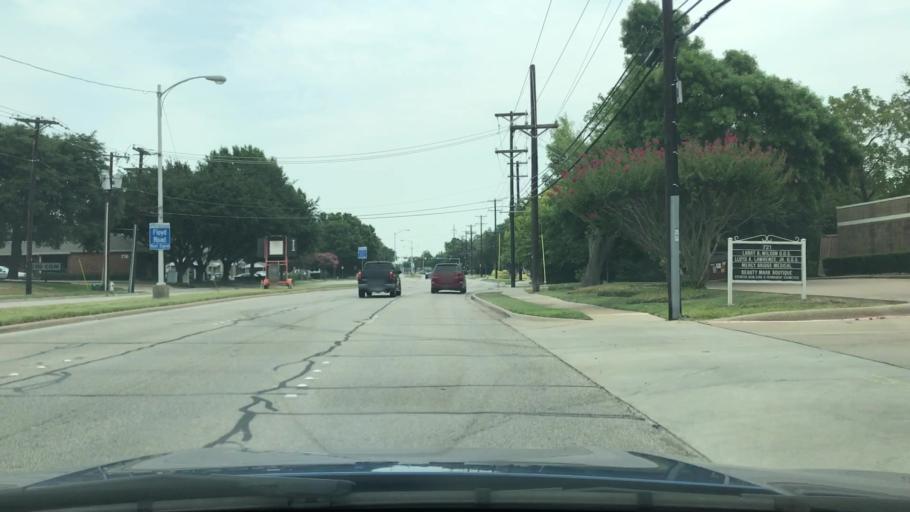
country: US
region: Texas
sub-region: Dallas County
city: Richardson
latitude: 32.9630
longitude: -96.7467
